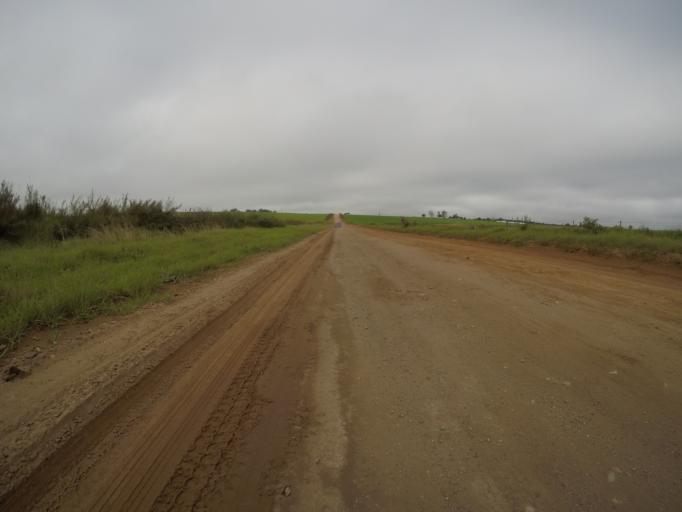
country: ZA
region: Eastern Cape
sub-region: Cacadu District Municipality
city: Kareedouw
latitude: -34.0262
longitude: 24.2420
